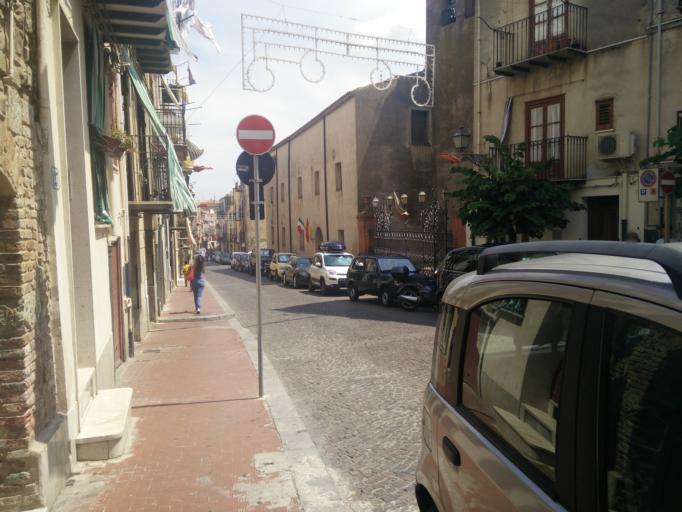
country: IT
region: Sicily
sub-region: Palermo
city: Castelbuono
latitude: 37.9308
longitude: 14.0862
